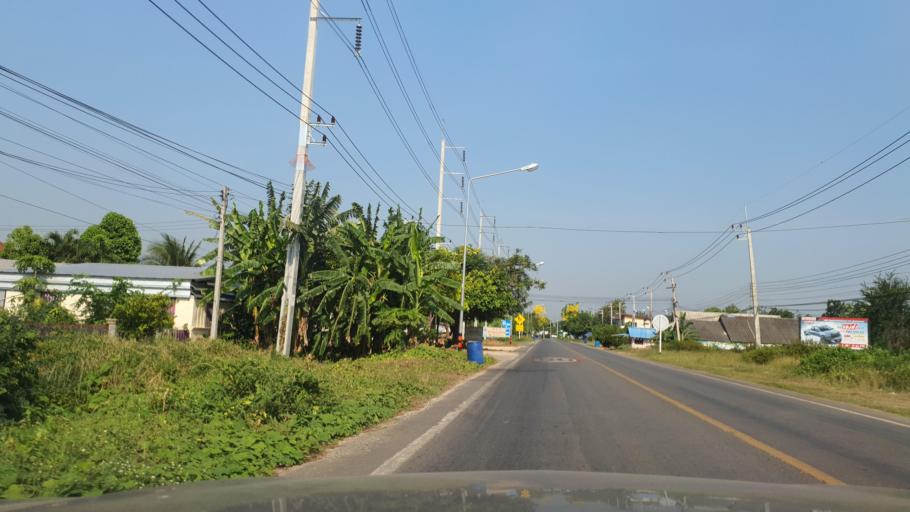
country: TH
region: Kanchanaburi
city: Kanchanaburi
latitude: 14.0351
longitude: 99.4955
